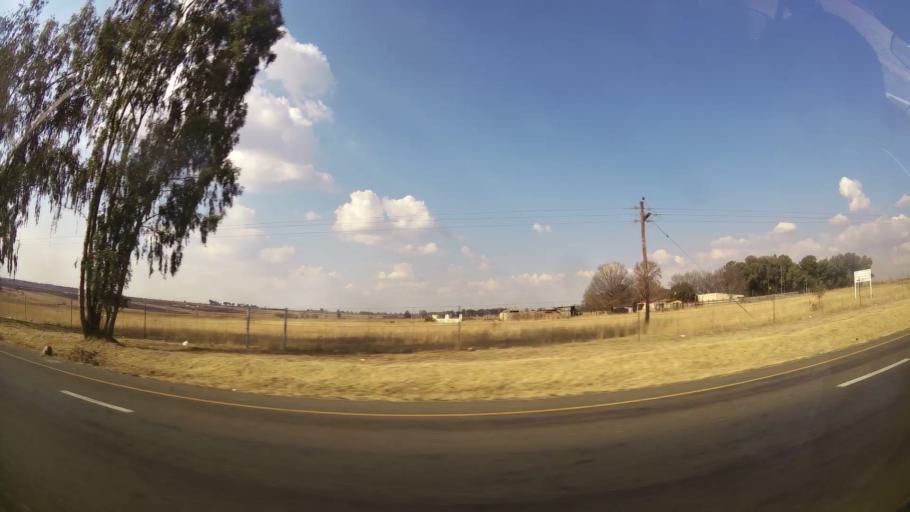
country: ZA
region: Gauteng
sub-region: Ekurhuleni Metropolitan Municipality
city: Brakpan
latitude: -26.3283
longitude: 28.3394
